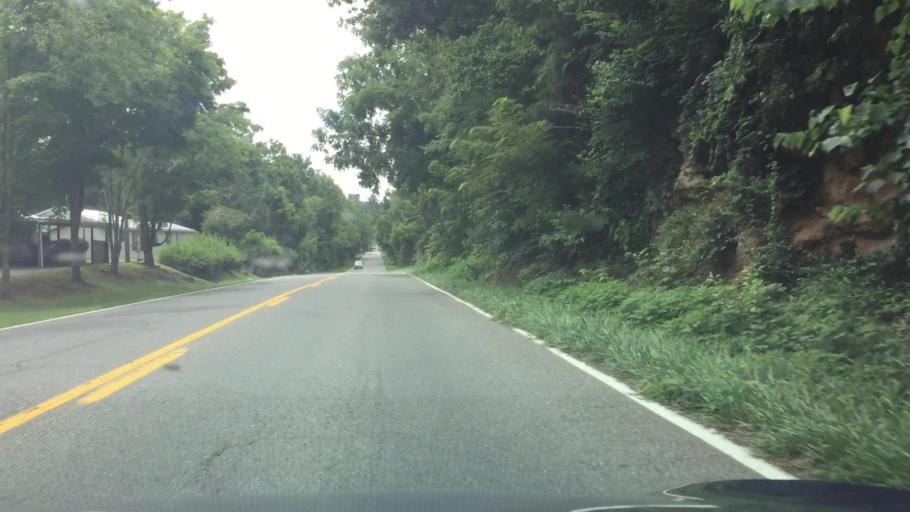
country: US
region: Virginia
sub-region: Pulaski County
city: Pulaski
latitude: 36.9497
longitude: -80.9092
